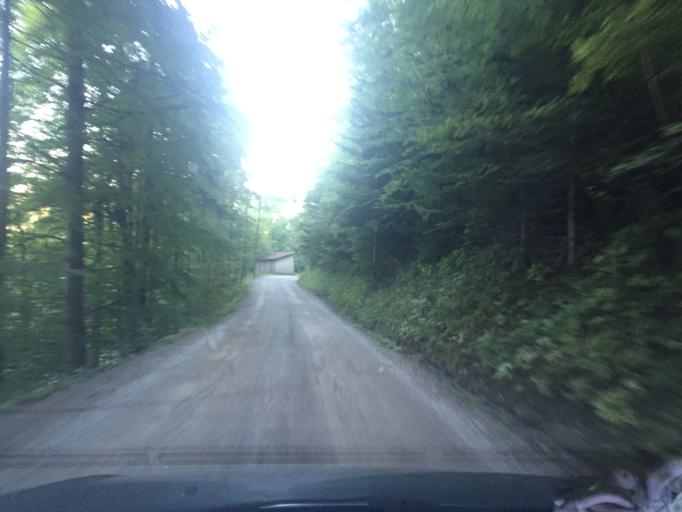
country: SI
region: Sostanj
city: Topolsica
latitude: 46.4587
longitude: 14.9976
